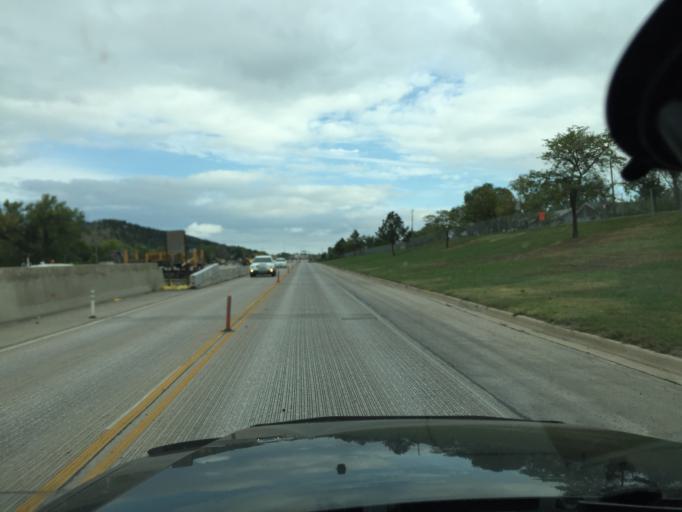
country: US
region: South Dakota
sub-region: Pennington County
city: Rapid City
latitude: 44.0907
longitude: -103.2322
